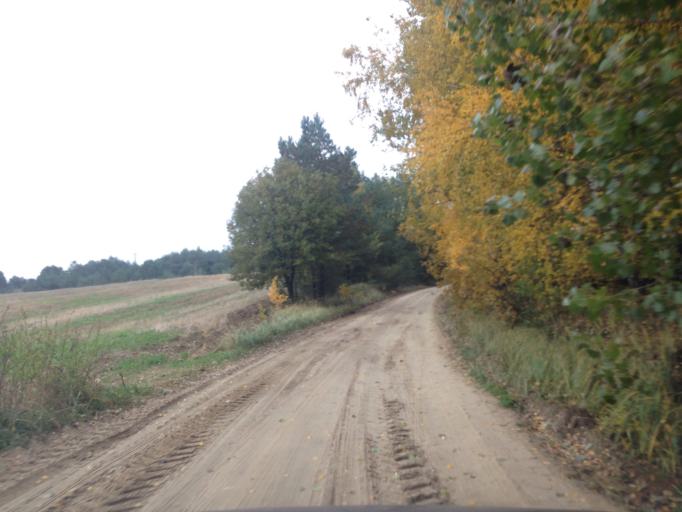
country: PL
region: Kujawsko-Pomorskie
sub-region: Powiat brodnicki
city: Brzozie
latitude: 53.3045
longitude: 19.6726
